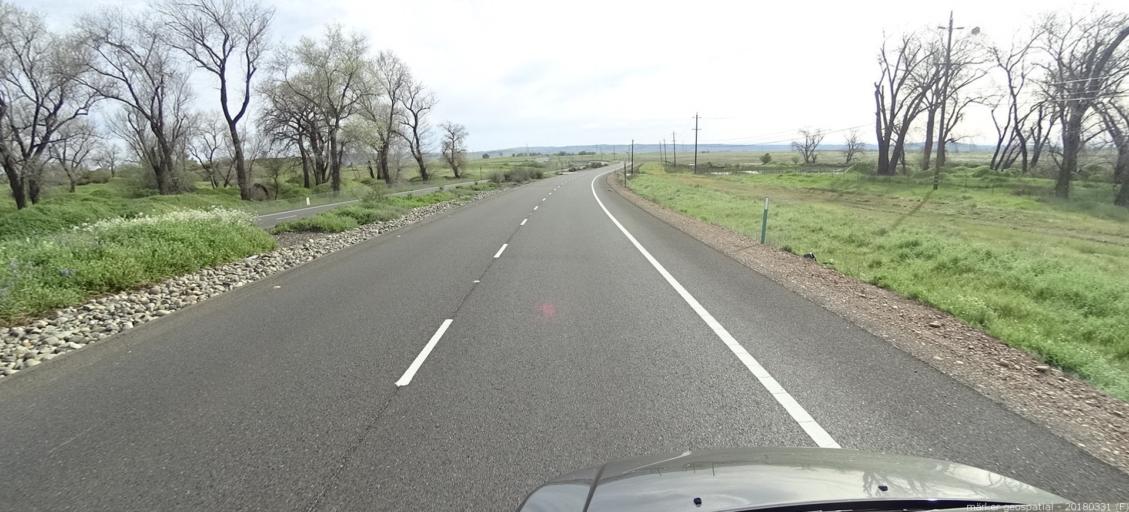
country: US
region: California
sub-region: Sacramento County
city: Folsom
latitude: 38.6108
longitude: -121.1615
